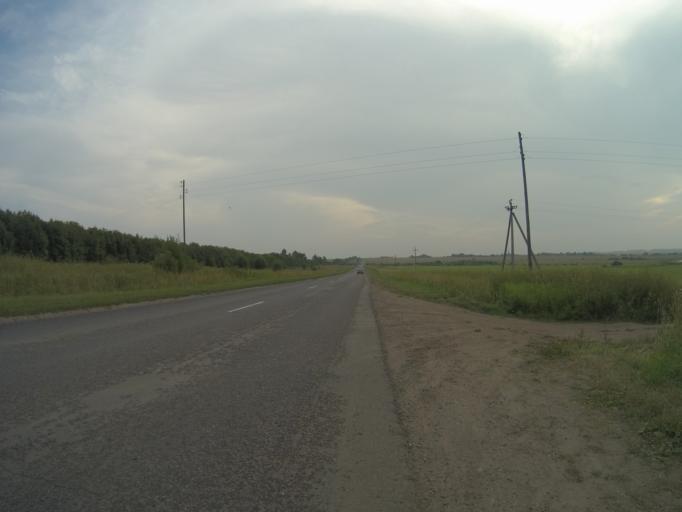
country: RU
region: Vladimir
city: Suzdal'
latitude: 56.3847
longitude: 40.2748
